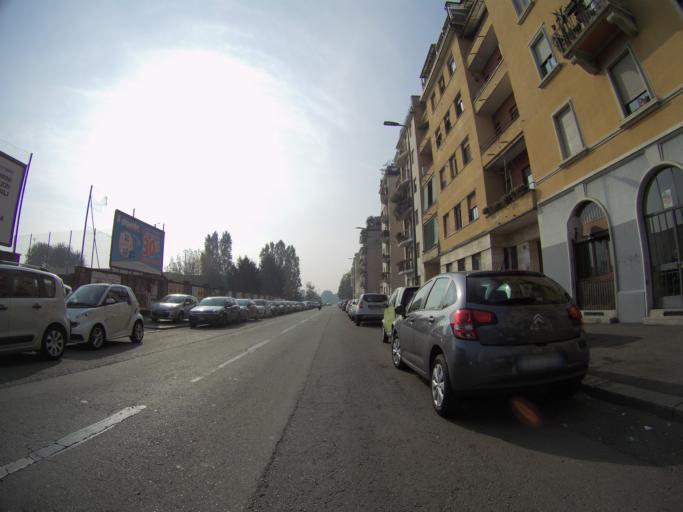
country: IT
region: Lombardy
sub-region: Citta metropolitana di Milano
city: Novegro-Tregarezzo-San Felice
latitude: 45.4807
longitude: 9.2366
